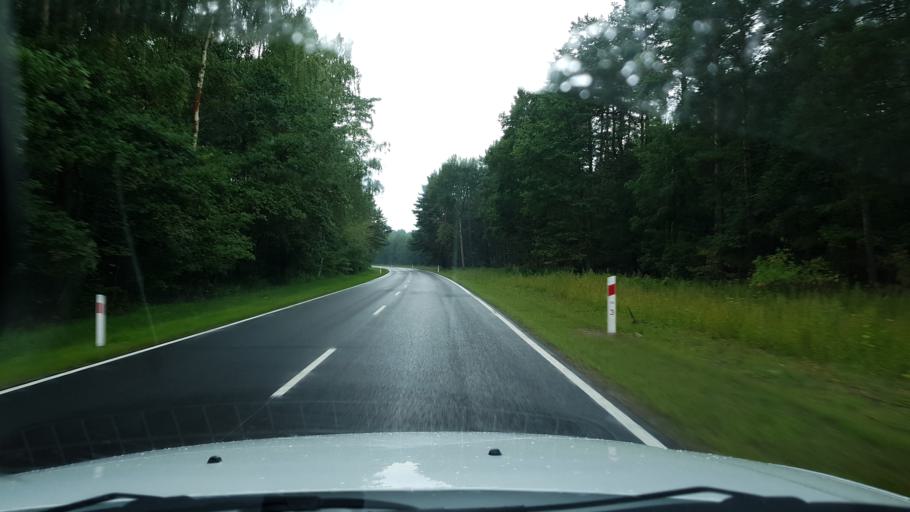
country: PL
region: West Pomeranian Voivodeship
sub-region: Powiat goleniowski
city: Mosty
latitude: 53.4407
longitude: 14.9367
